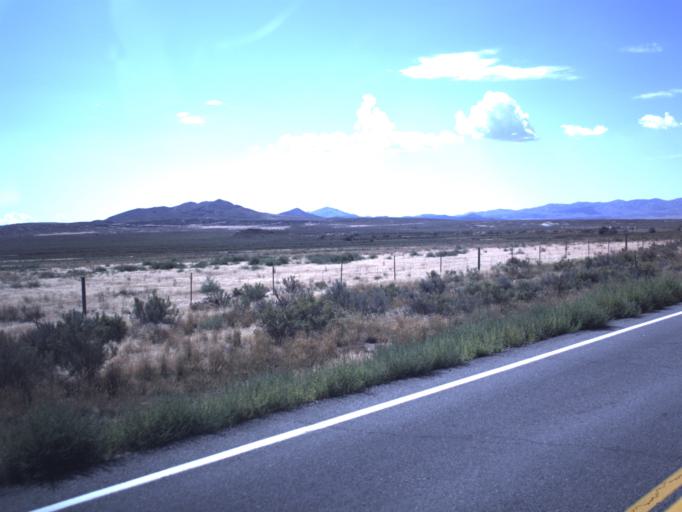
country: US
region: Utah
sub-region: Tooele County
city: Tooele
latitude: 40.1912
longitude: -112.4166
